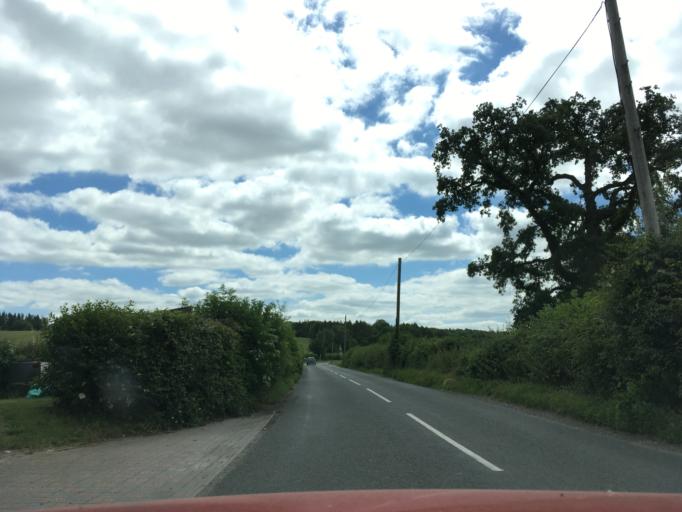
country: GB
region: England
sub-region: Hampshire
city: Highclere
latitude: 51.2381
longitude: -1.3845
